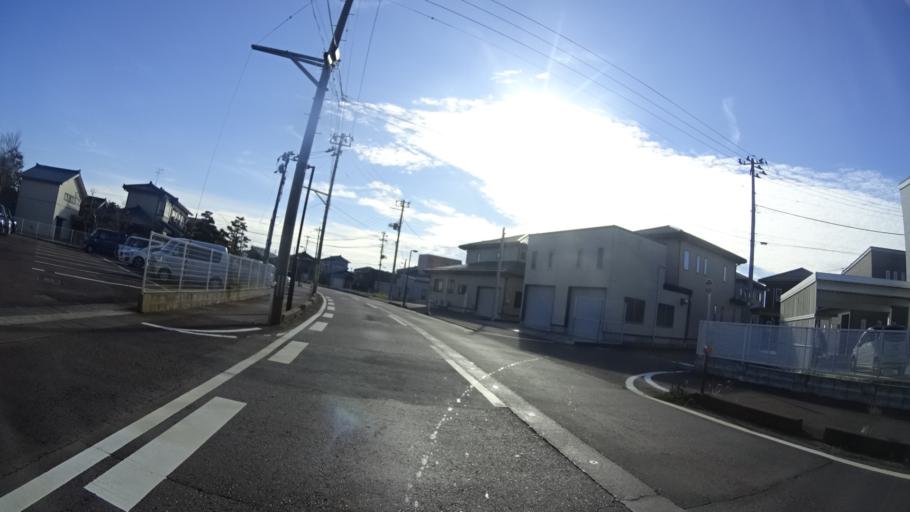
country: JP
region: Niigata
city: Yoshida-kasugacho
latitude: 37.6235
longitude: 138.8387
